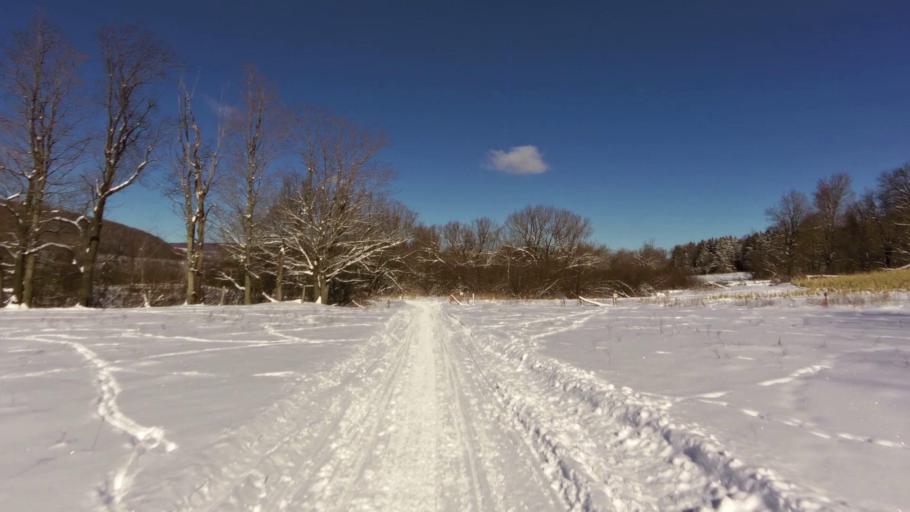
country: US
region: New York
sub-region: Chautauqua County
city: Fredonia
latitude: 42.3477
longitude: -79.1709
